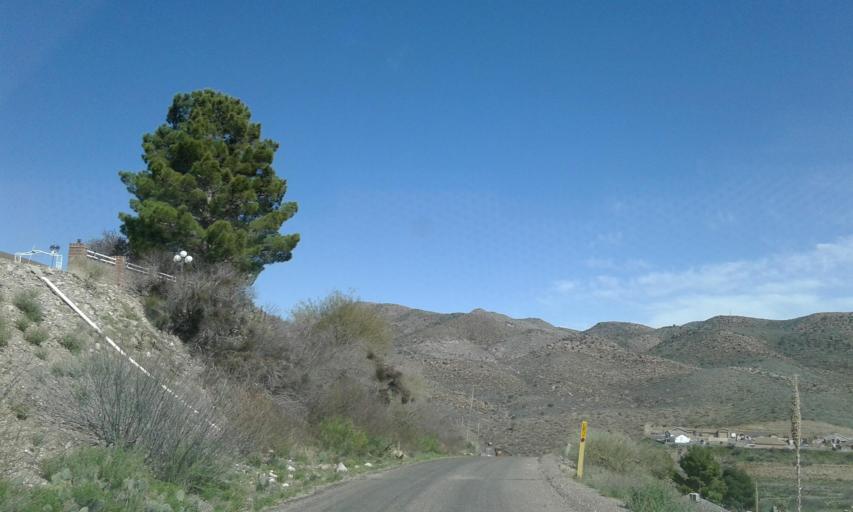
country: US
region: Arizona
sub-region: Gila County
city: Central Heights-Midland City
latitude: 33.4253
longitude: -110.8152
